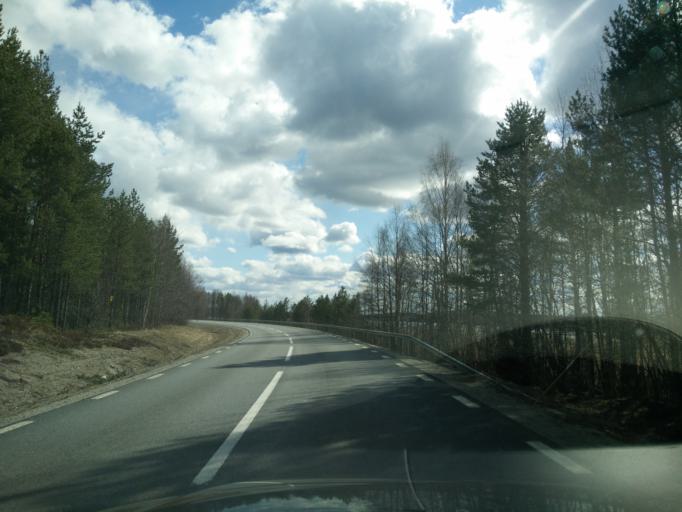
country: SE
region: Jaemtland
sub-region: Braecke Kommun
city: Braecke
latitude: 62.4548
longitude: 14.9681
